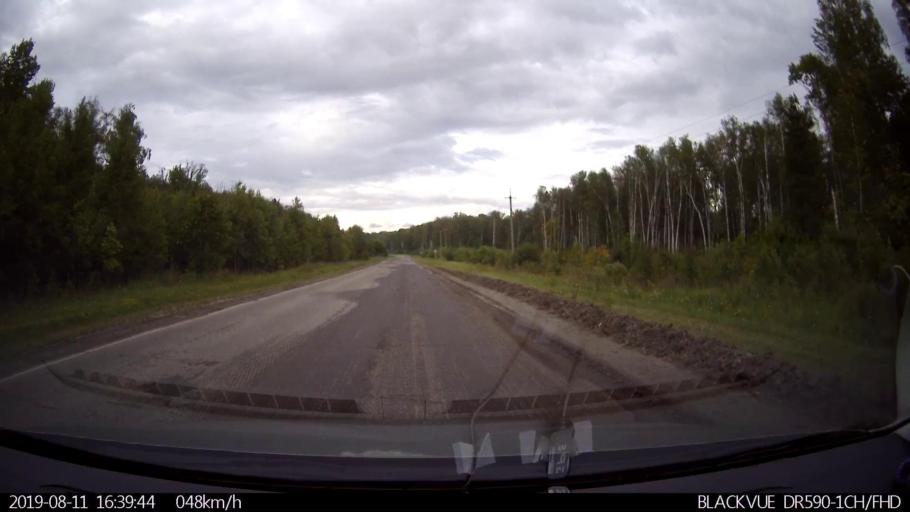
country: RU
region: Ulyanovsk
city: Mayna
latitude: 54.1417
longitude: 47.6398
